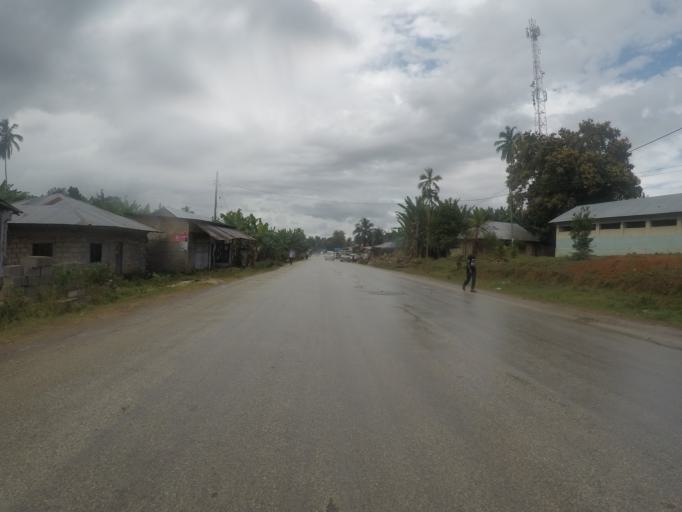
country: TZ
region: Zanzibar Central/South
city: Koani
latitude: -6.0421
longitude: 39.2289
